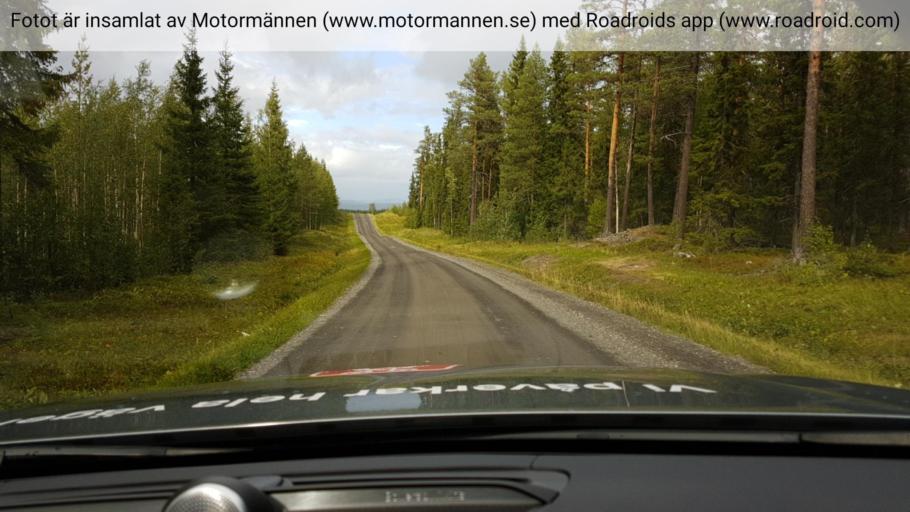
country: SE
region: Jaemtland
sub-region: OEstersunds Kommun
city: Lit
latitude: 63.7484
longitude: 14.6530
